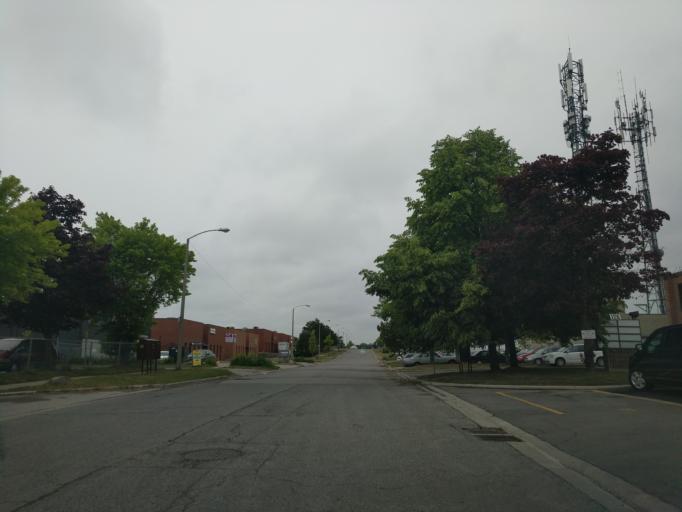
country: CA
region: Ontario
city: Markham
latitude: 43.8320
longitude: -79.2561
